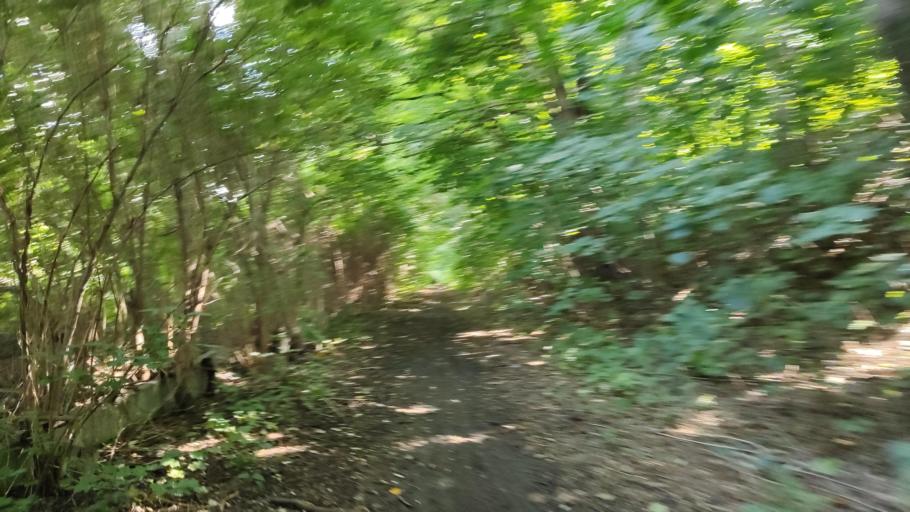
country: PL
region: Lower Silesian Voivodeship
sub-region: Powiat wroclawski
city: Wroclaw
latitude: 51.0776
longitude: 17.0032
